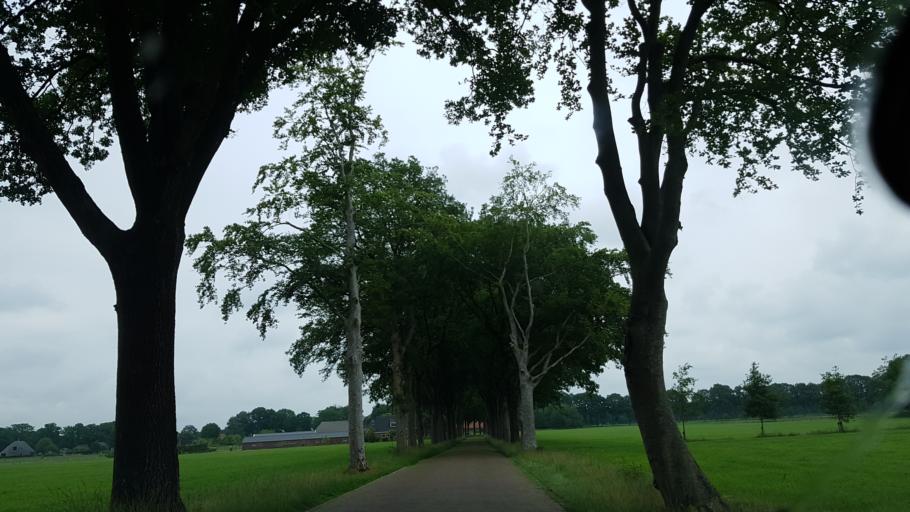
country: NL
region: Drenthe
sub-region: Gemeente Tynaarlo
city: Tynaarlo
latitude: 53.0498
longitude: 6.6314
